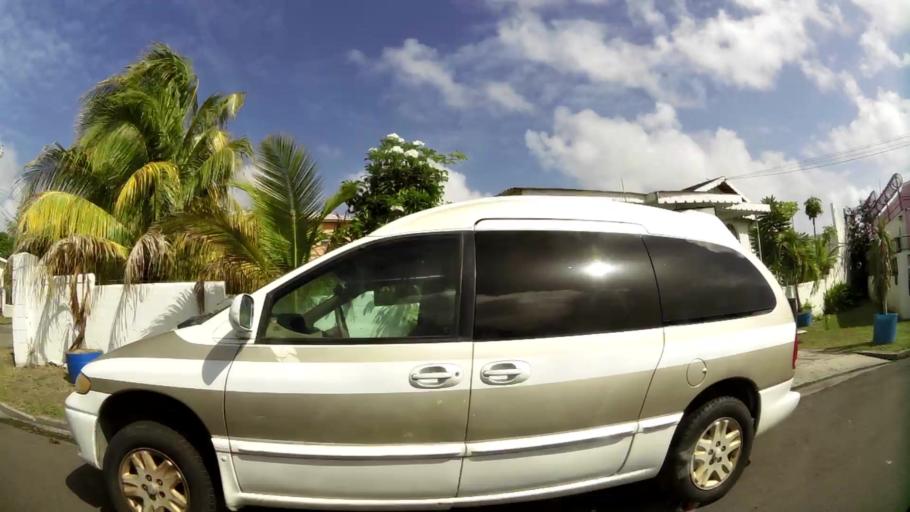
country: KN
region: Saint George Basseterre
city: Basseterre
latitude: 17.2999
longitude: -62.7287
